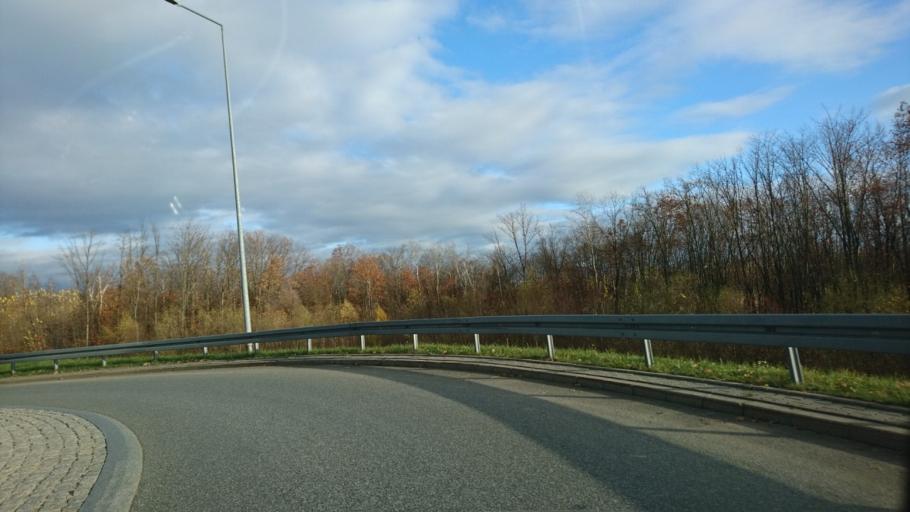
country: PL
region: Silesian Voivodeship
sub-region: Powiat zywiecki
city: Lodygowice
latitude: 49.7119
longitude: 19.1230
